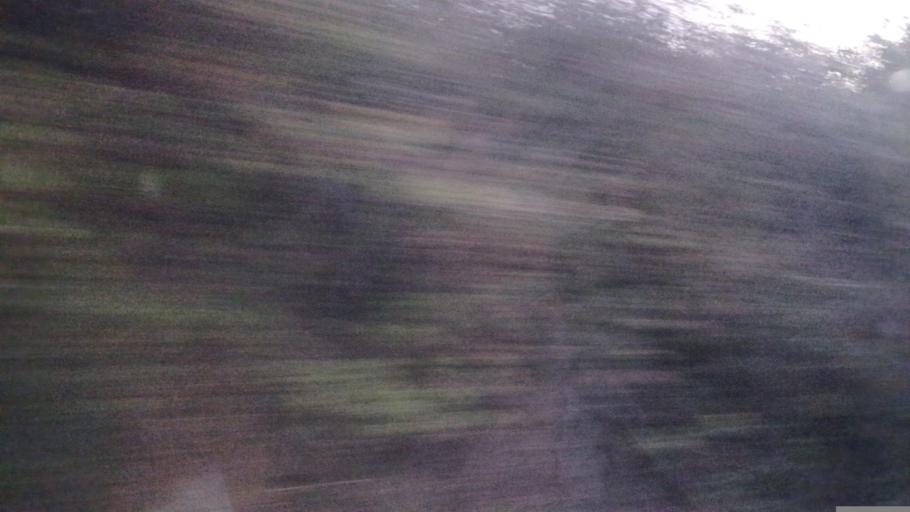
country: CY
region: Pafos
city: Mesogi
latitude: 34.8455
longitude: 32.5259
